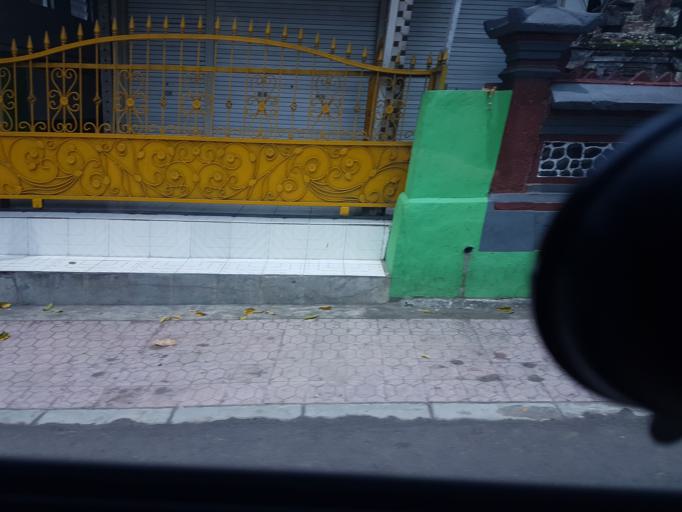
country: ID
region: Bali
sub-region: Kabupaten Gianyar
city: Ubud
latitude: -8.5222
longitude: 115.2927
